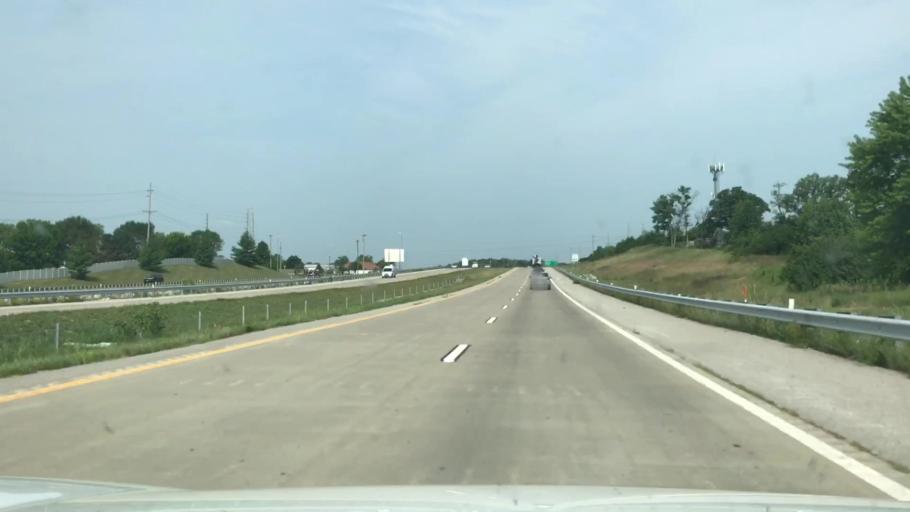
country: US
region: Missouri
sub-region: Saint Charles County
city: Dardenne Prairie
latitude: 38.7573
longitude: -90.7097
